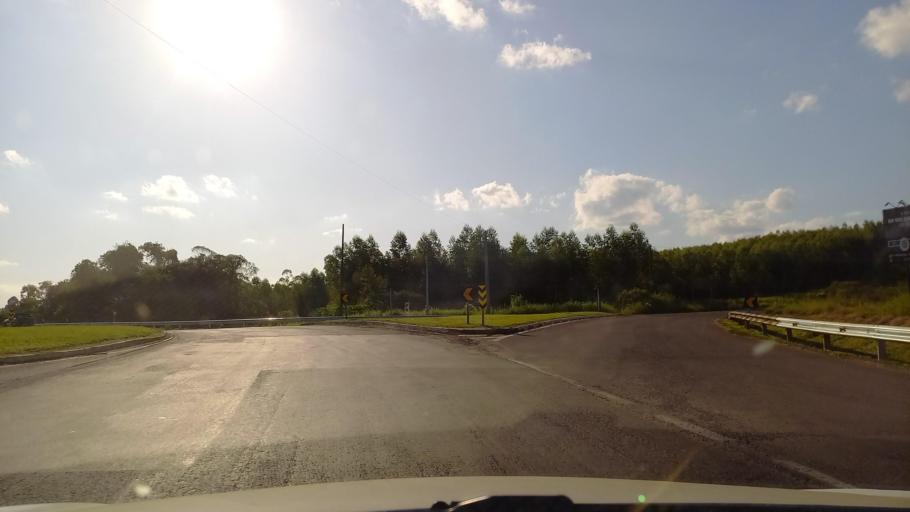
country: BR
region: Rio Grande do Sul
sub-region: Taquari
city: Taquari
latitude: -29.7037
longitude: -51.7919
